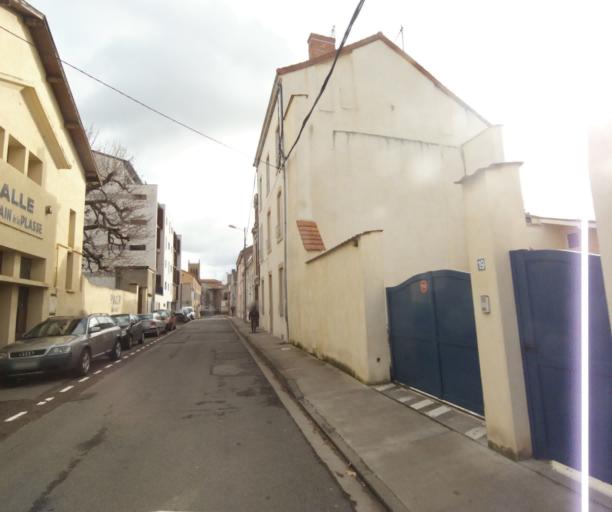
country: FR
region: Rhone-Alpes
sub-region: Departement de la Loire
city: Roanne
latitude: 46.0402
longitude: 4.0688
